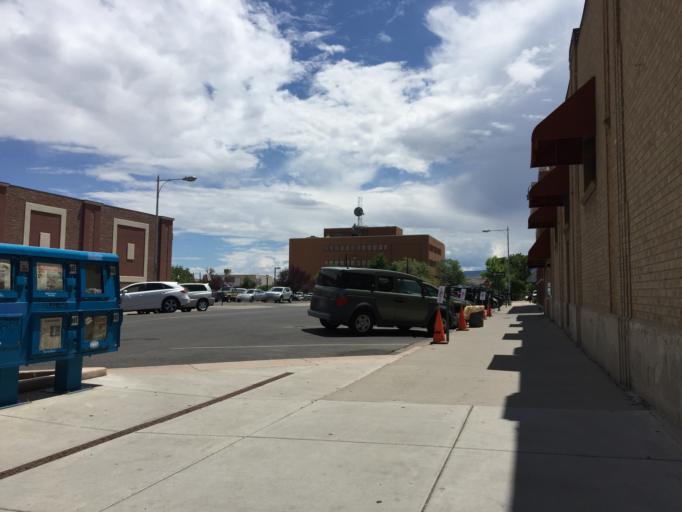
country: US
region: Colorado
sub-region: Mesa County
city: Grand Junction
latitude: 39.0672
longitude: -108.5629
